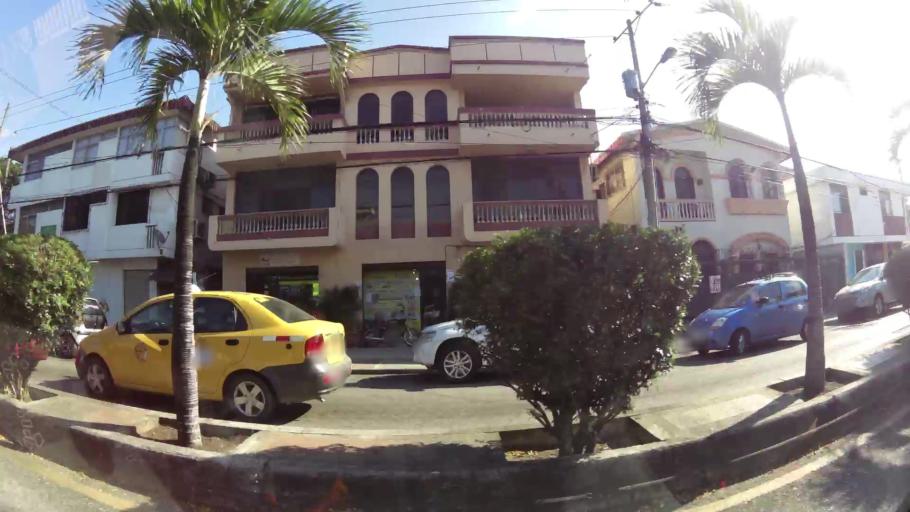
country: EC
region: Guayas
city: Guayaquil
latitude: -2.1750
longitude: -79.8978
